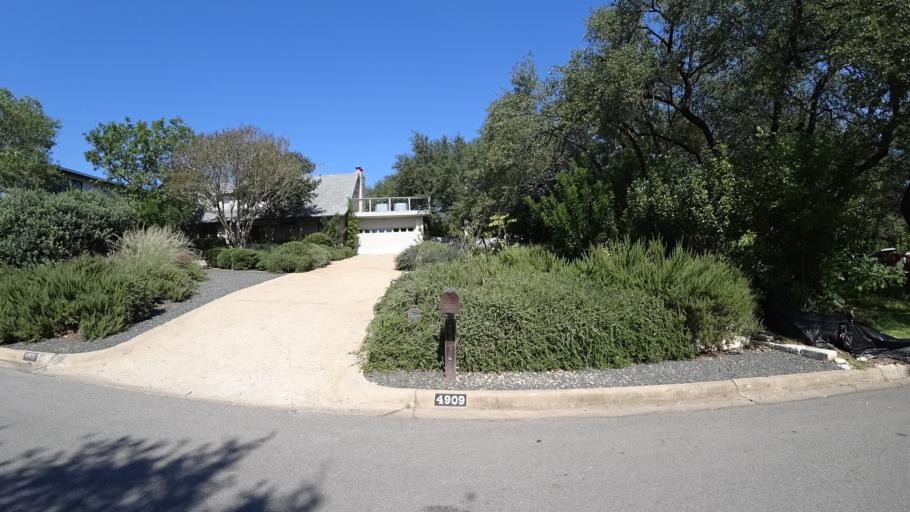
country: US
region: Texas
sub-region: Travis County
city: Rollingwood
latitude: 30.2730
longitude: -97.7904
